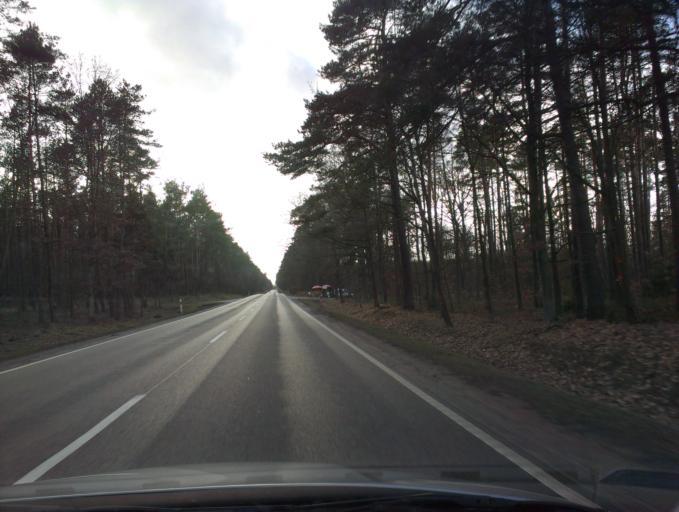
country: PL
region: Pomeranian Voivodeship
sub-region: Powiat czluchowski
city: Czluchow
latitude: 53.6481
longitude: 17.3108
